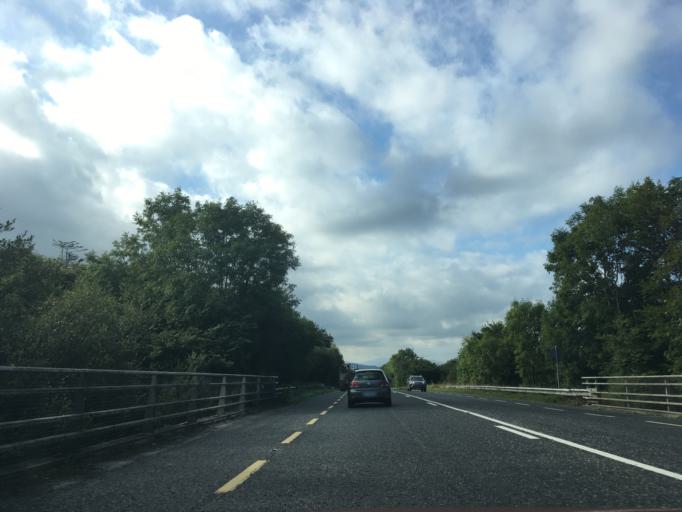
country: IE
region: Leinster
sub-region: Loch Garman
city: Loch Garman
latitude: 52.3276
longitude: -6.5055
